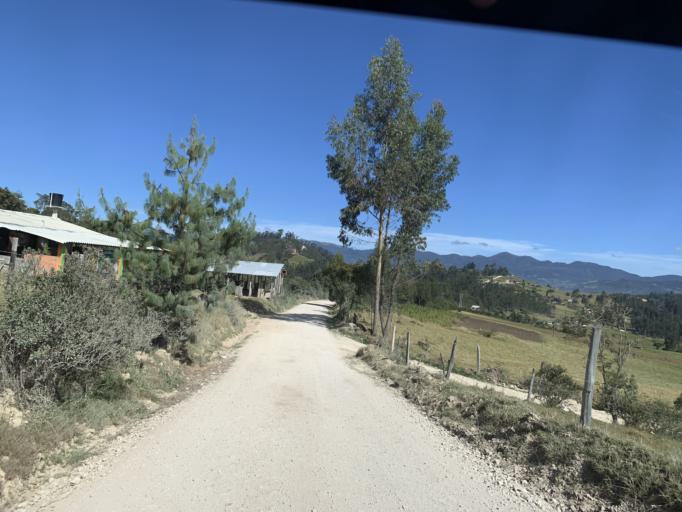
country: CO
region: Boyaca
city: Tuta
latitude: 5.7052
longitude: -73.1505
